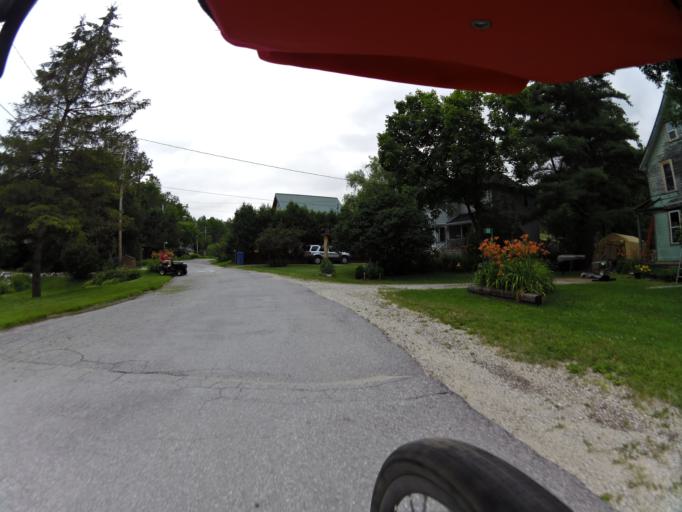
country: CA
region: Quebec
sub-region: Outaouais
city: Wakefield
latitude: 45.6831
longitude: -75.9292
